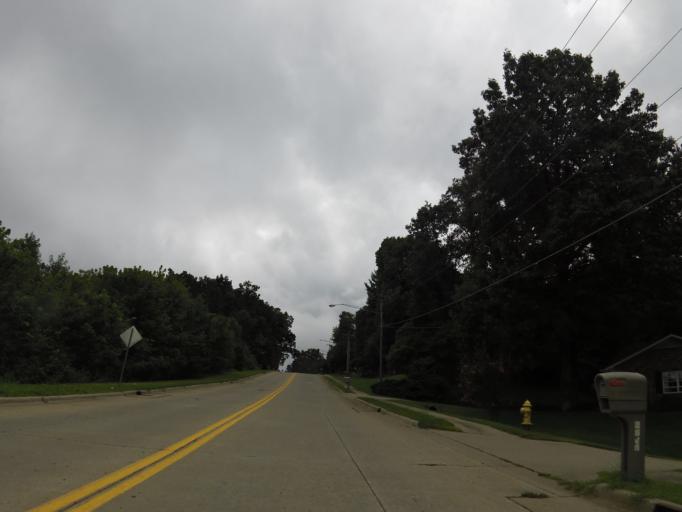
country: US
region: Missouri
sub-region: Cape Girardeau County
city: Cape Girardeau
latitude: 37.3464
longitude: -89.5590
